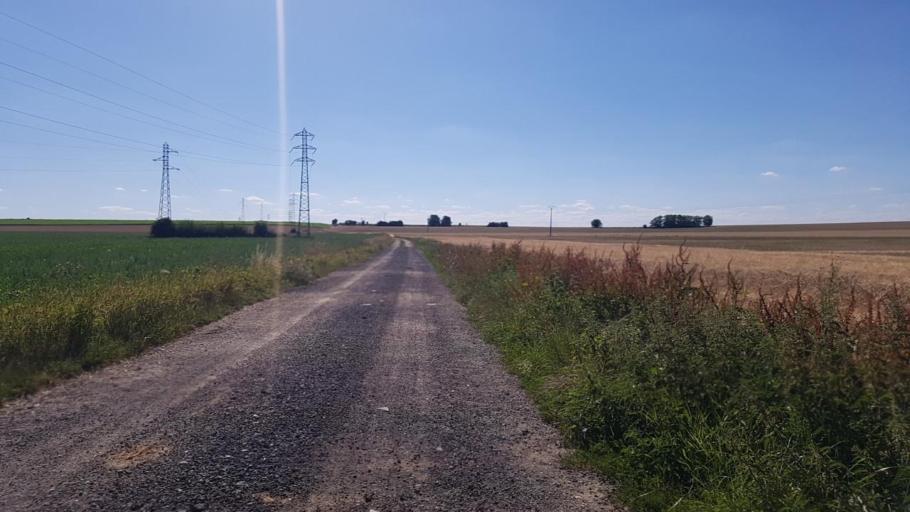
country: FR
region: Ile-de-France
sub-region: Departement de Seine-et-Marne
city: Chauconin-Neufmontiers
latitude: 48.9523
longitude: 2.8380
